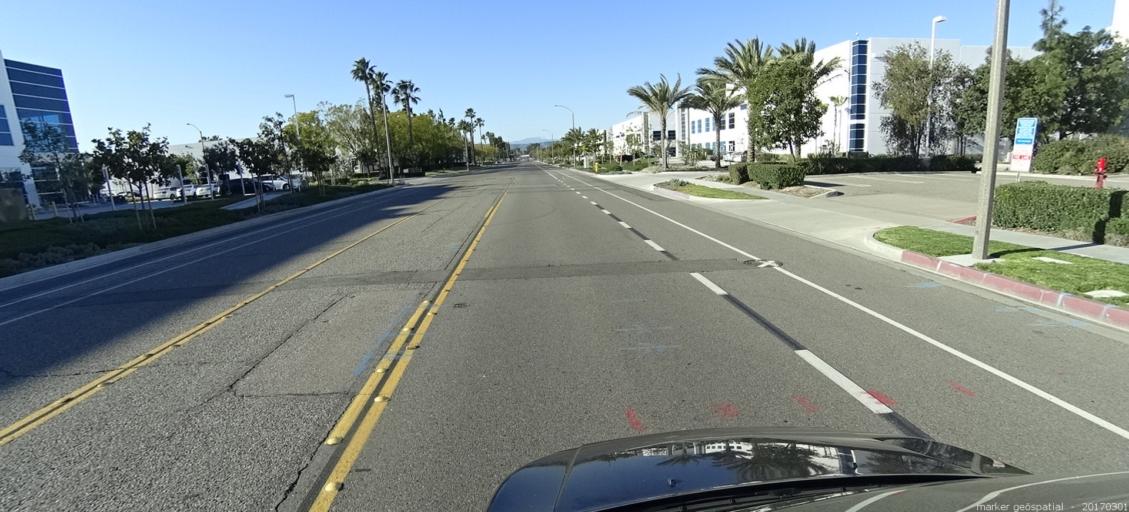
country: US
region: California
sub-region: Orange County
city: Placentia
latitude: 33.8554
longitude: -117.8475
